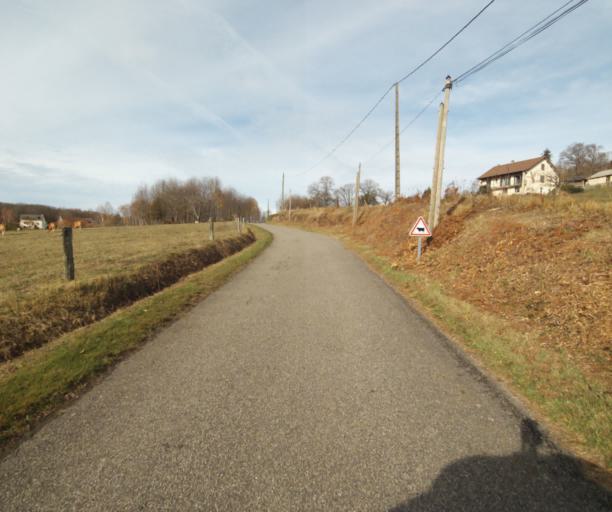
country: FR
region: Limousin
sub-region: Departement de la Correze
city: Sainte-Fortunade
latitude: 45.1845
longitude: 1.7410
